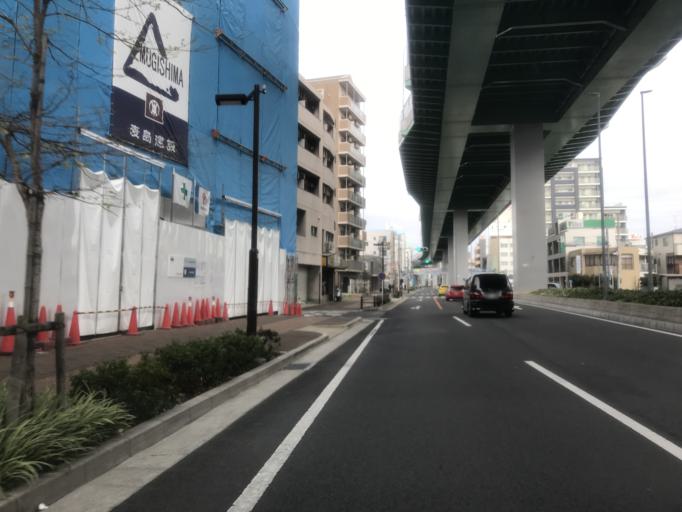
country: JP
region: Aichi
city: Nagoya-shi
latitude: 35.1864
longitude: 136.8906
